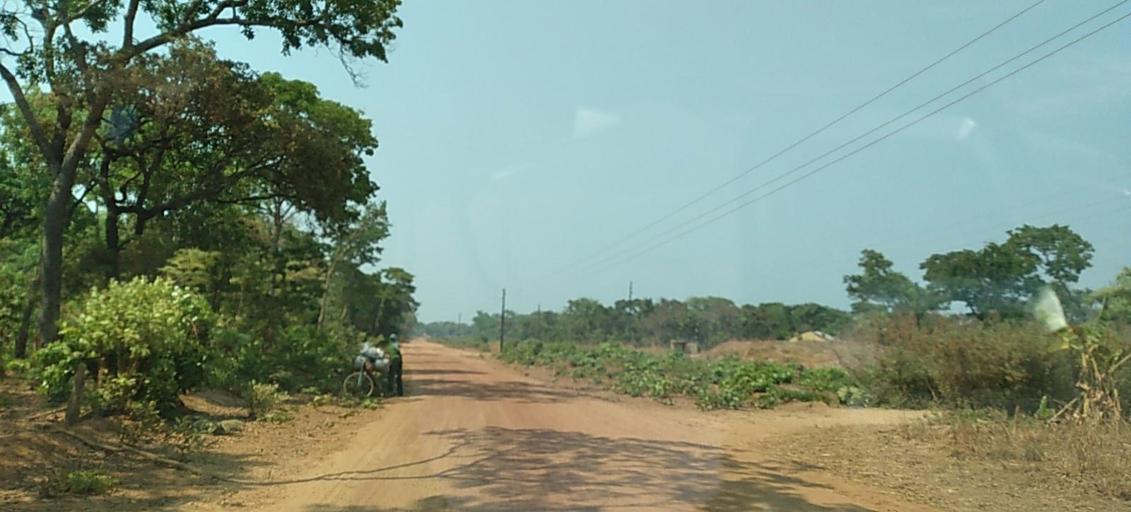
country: ZM
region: Copperbelt
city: Kalulushi
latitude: -13.1007
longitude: 27.4044
